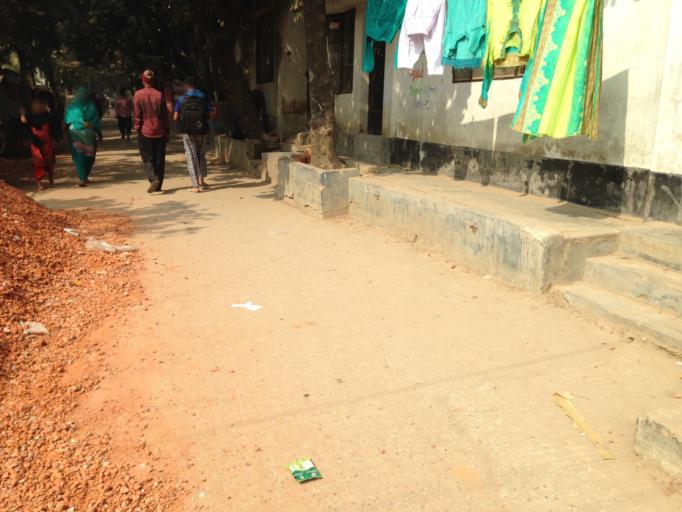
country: BD
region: Dhaka
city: Azimpur
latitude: 23.8069
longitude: 90.3809
